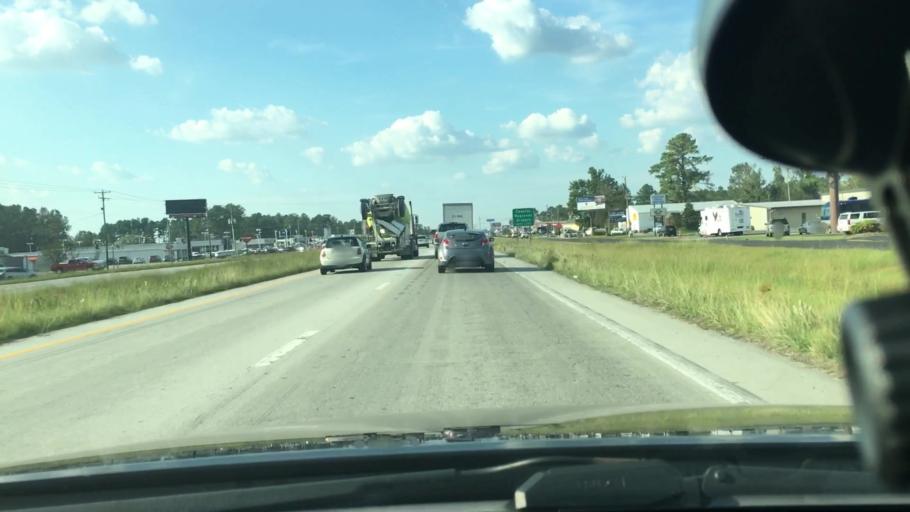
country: US
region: North Carolina
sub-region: Craven County
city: James City
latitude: 35.0711
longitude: -77.0258
